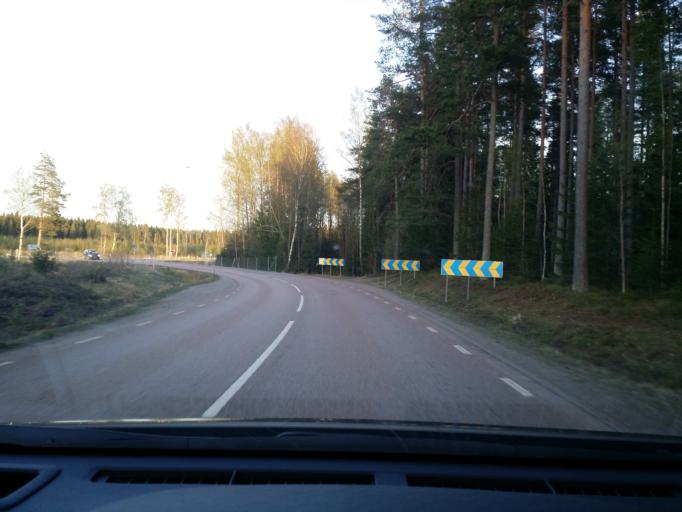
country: SE
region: Vaestmanland
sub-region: Sala Kommun
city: Sala
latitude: 59.8021
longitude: 16.5562
